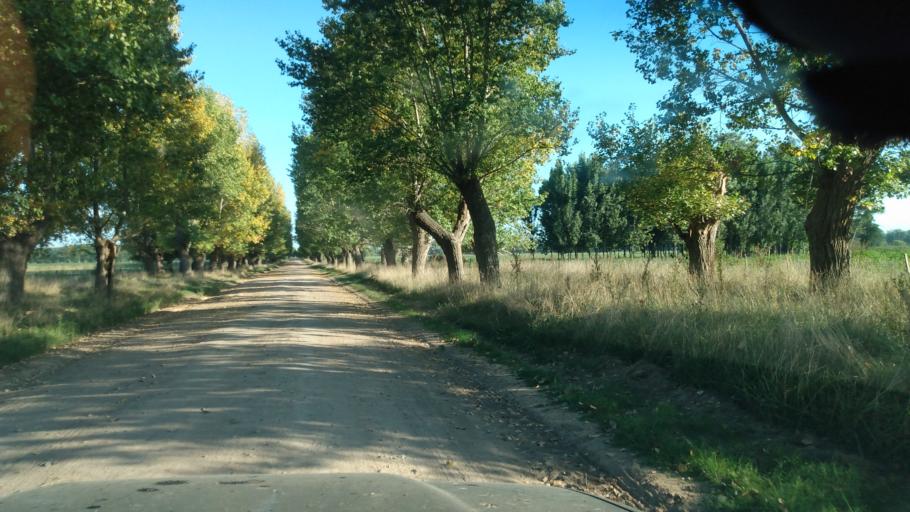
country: AR
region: Buenos Aires
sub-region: Partido de Lujan
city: Lujan
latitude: -34.5891
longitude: -59.0737
